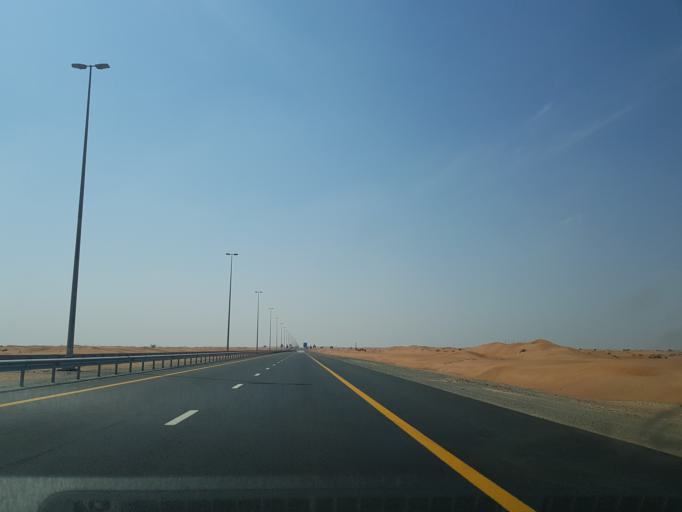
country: AE
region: Ash Shariqah
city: Adh Dhayd
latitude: 25.2547
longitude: 55.7473
